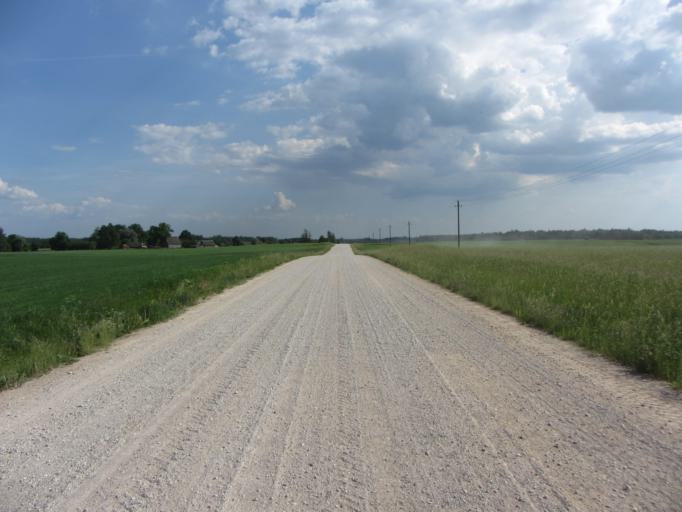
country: LT
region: Kauno apskritis
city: Jonava
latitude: 55.1814
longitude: 24.3753
